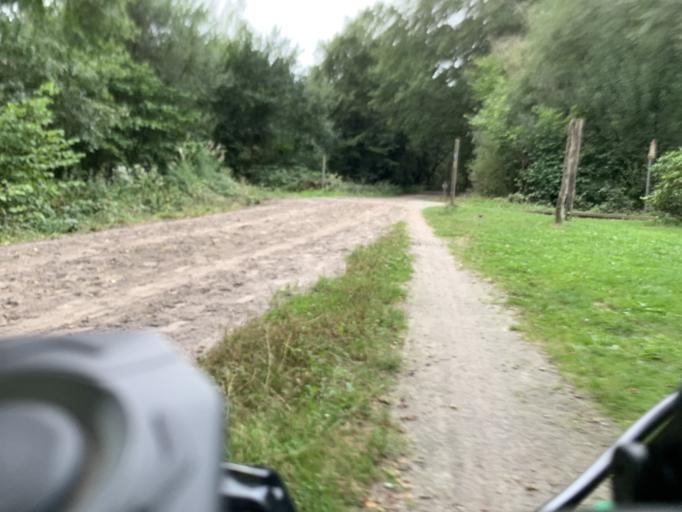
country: DE
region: Lower Saxony
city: Westerstede
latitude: 53.2322
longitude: 7.9252
